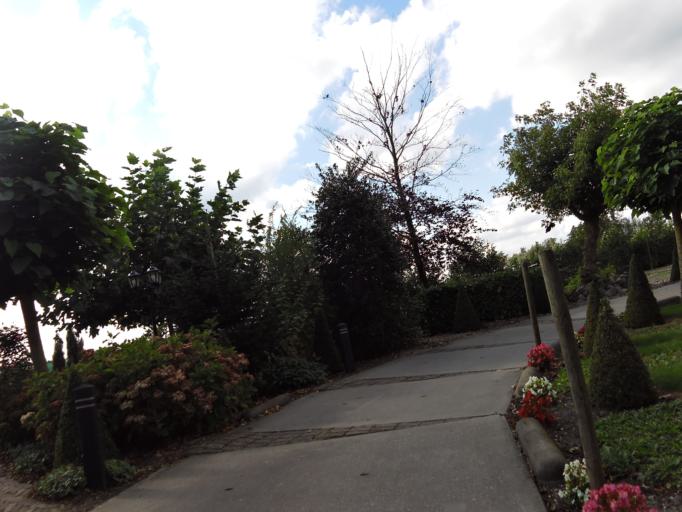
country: NL
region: South Holland
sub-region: Gemeente Boskoop
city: Boskoop
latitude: 52.1010
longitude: 4.6180
